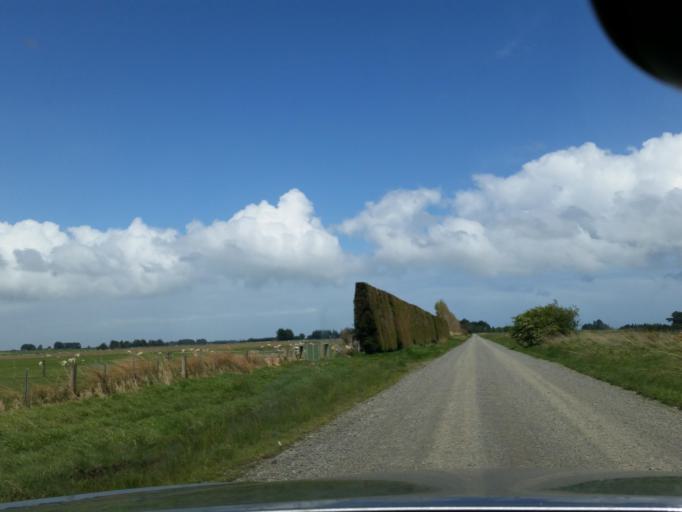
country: NZ
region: Southland
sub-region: Southland District
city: Riverton
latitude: -46.2065
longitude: 168.0783
